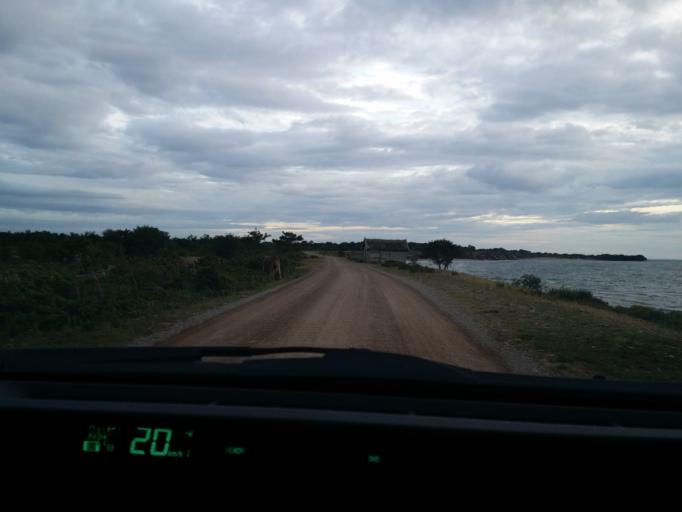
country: SE
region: Kalmar
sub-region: Borgholms Kommun
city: Borgholm
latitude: 57.2093
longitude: 16.9353
